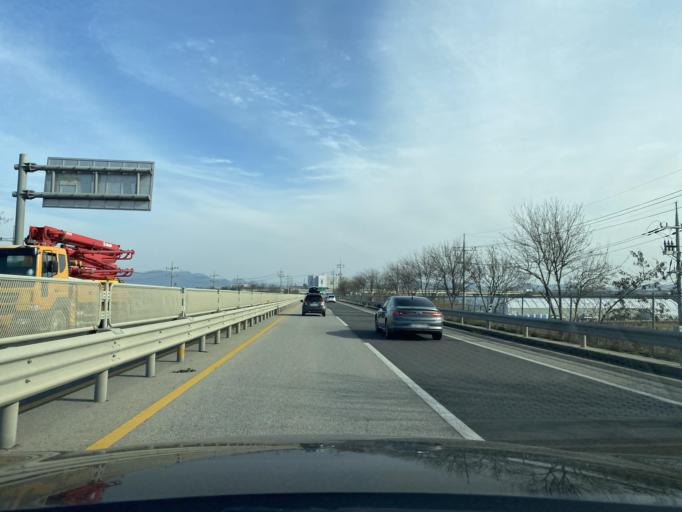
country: KR
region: Chungcheongnam-do
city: Yesan
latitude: 36.6868
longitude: 126.7648
